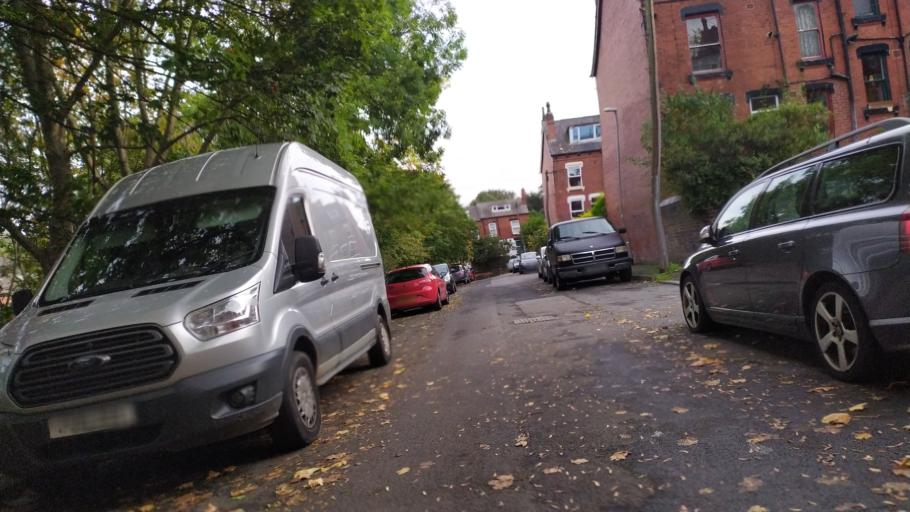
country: GB
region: England
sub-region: City and Borough of Leeds
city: Chapel Allerton
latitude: 53.8176
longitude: -1.5504
